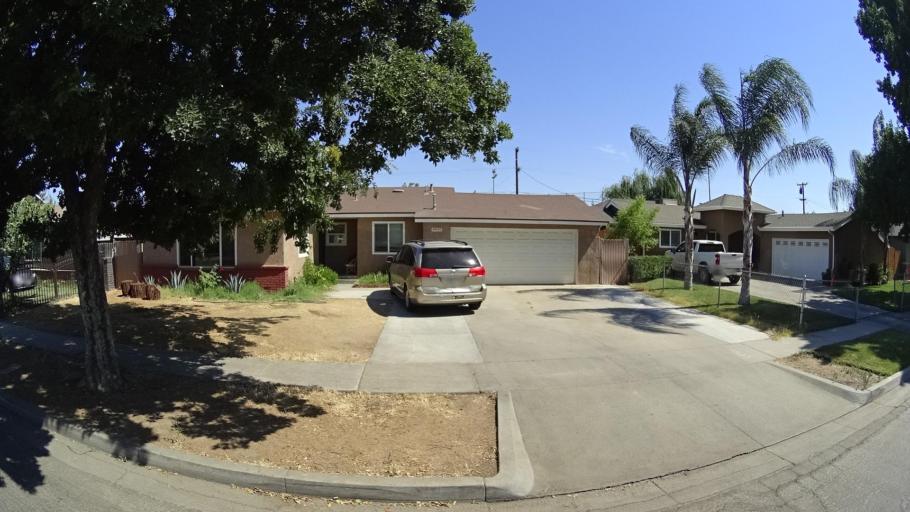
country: US
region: California
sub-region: Fresno County
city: Fresno
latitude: 36.7259
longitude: -119.7439
